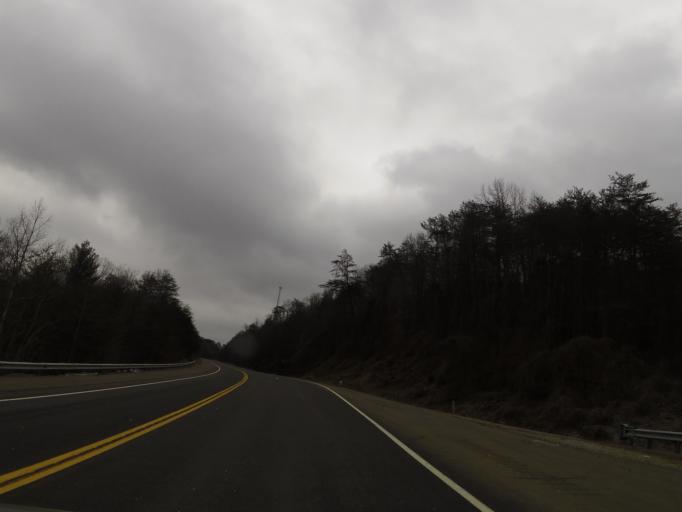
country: US
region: Tennessee
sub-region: Scott County
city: Huntsville
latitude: 36.4033
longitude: -84.4497
